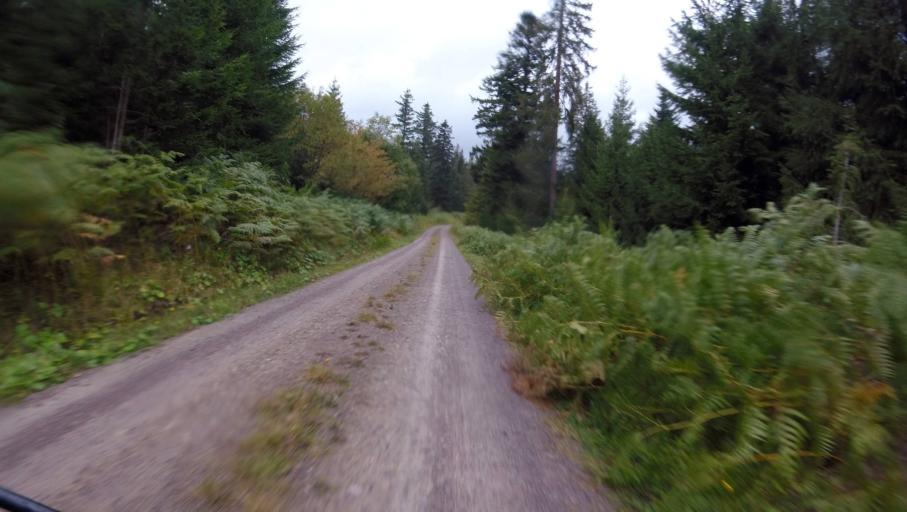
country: DE
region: Baden-Wuerttemberg
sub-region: Karlsruhe Region
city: Enzklosterle
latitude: 48.6695
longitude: 8.4218
